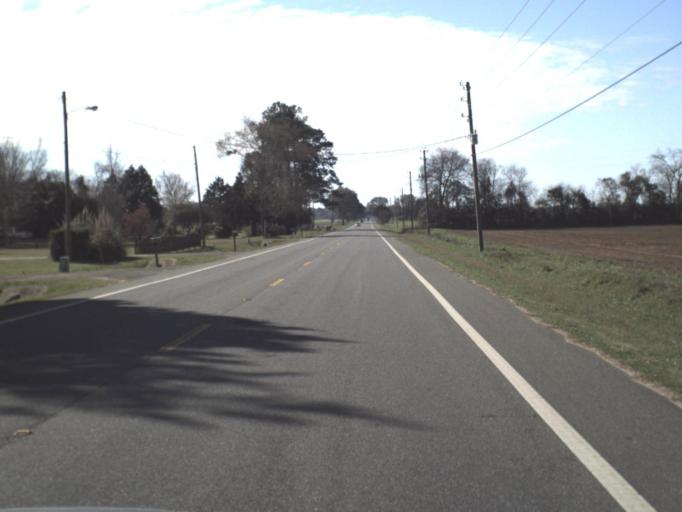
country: US
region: Florida
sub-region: Jackson County
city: Malone
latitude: 30.8579
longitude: -85.1637
